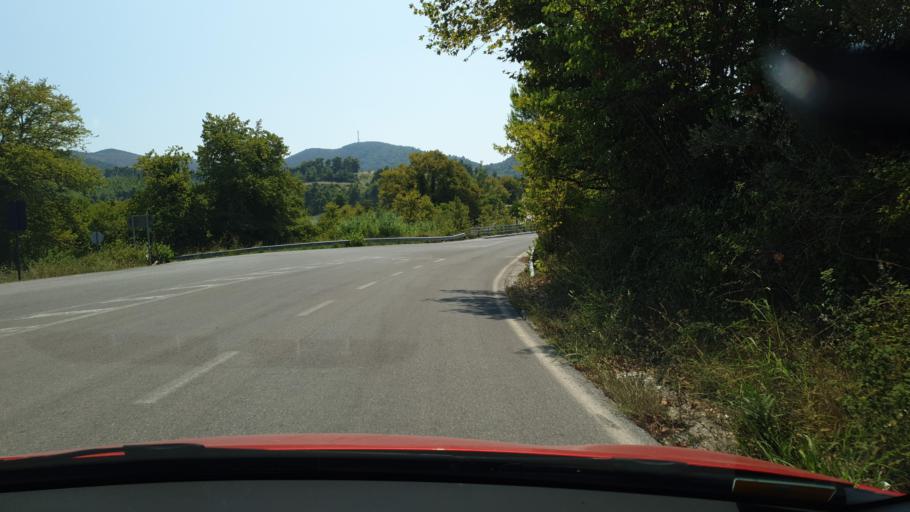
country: GR
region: Central Greece
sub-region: Nomos Evvoias
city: Kymi
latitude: 38.6024
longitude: 24.0755
